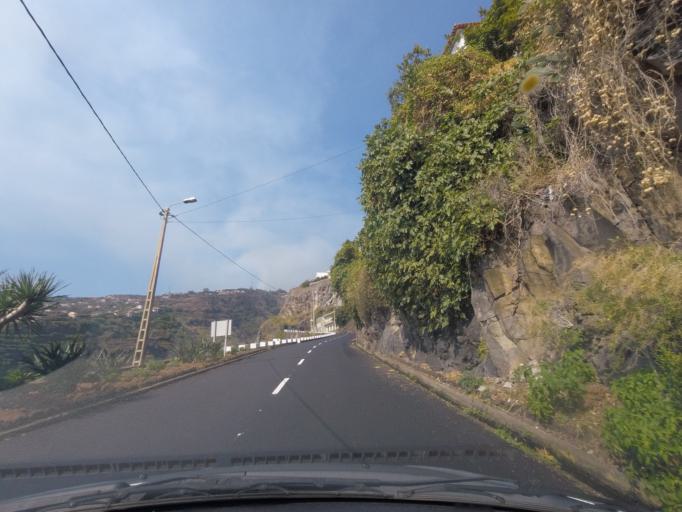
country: PT
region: Madeira
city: Ribeira Brava
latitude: 32.6705
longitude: -17.0624
